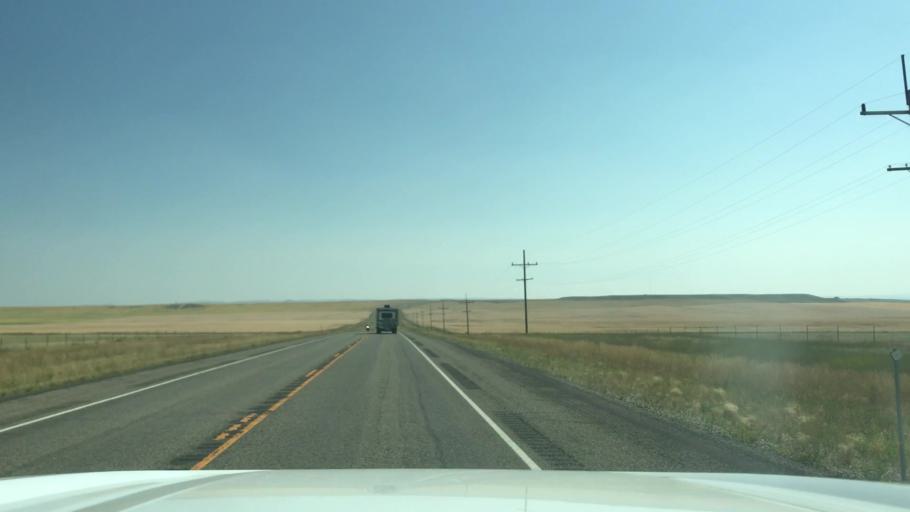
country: US
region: Montana
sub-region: Wheatland County
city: Harlowton
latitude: 46.4935
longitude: -109.7661
